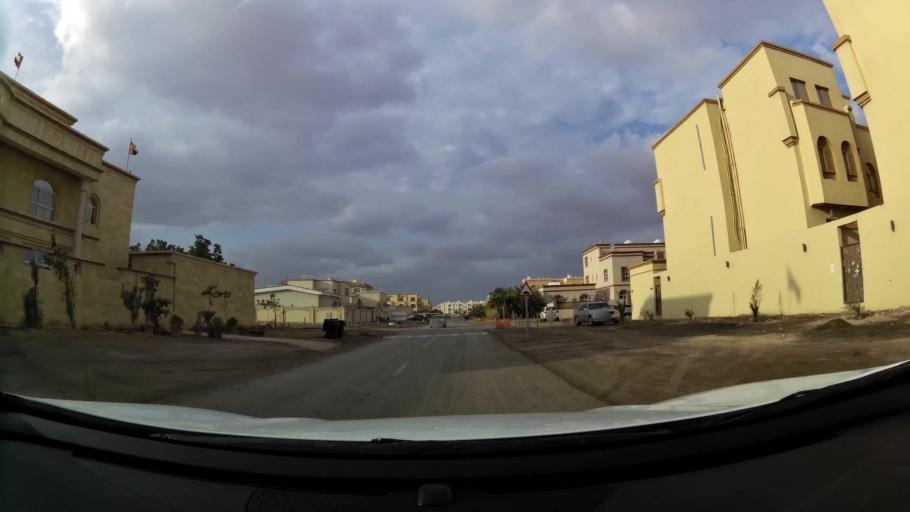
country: AE
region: Abu Dhabi
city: Abu Dhabi
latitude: 24.3533
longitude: 54.5515
